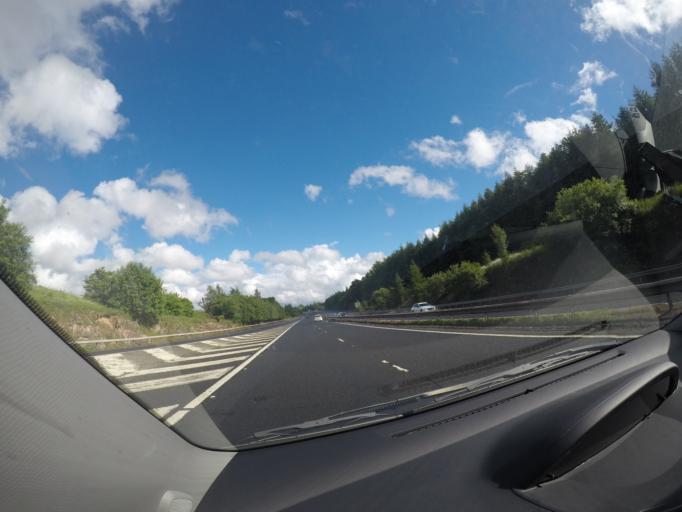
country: GB
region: Scotland
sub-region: South Lanarkshire
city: Lesmahagow
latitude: 55.6489
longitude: -3.8890
